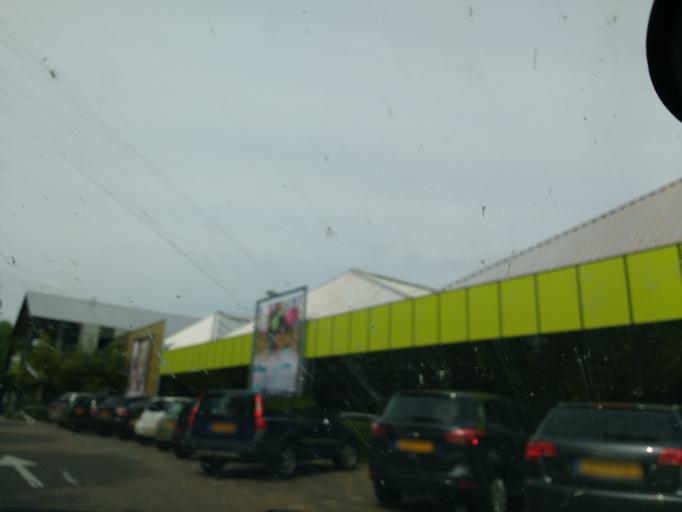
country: NL
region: Gelderland
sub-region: Gemeente Nijmegen
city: Nijmegen
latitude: 51.7949
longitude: 5.8495
